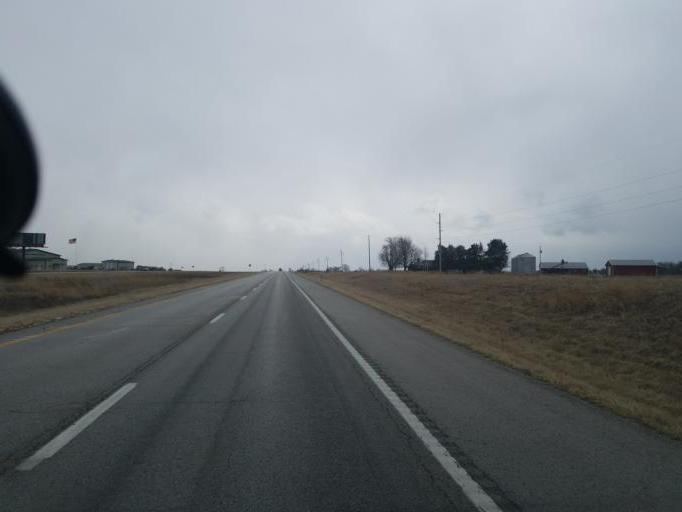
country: US
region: Missouri
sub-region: Randolph County
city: Moberly
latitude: 39.5439
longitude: -92.4513
